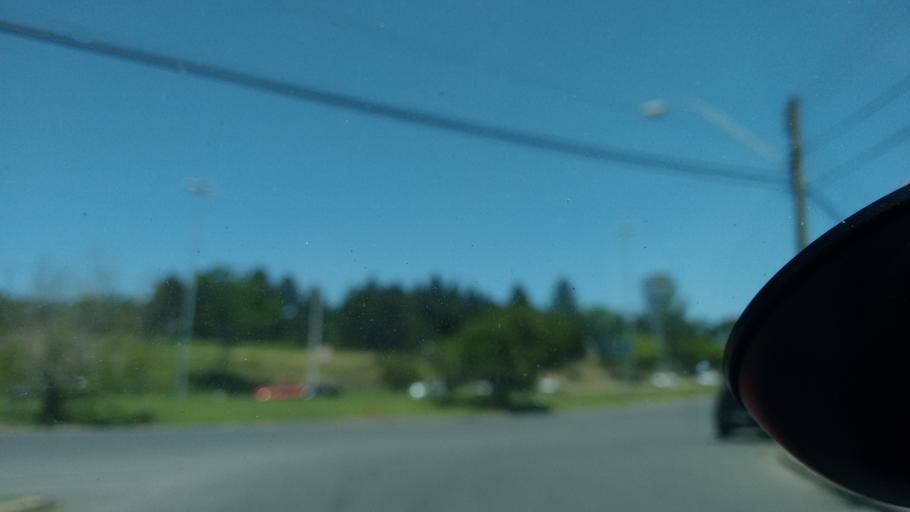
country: BR
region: Rio Grande do Sul
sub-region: Cachoeirinha
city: Cachoeirinha
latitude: -30.0015
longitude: -51.1282
